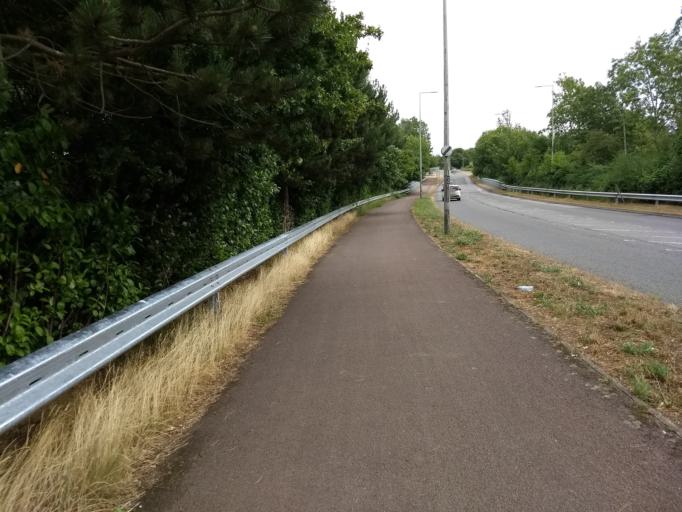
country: GB
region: England
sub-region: Milton Keynes
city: Bradwell
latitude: 52.0580
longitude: -0.7940
